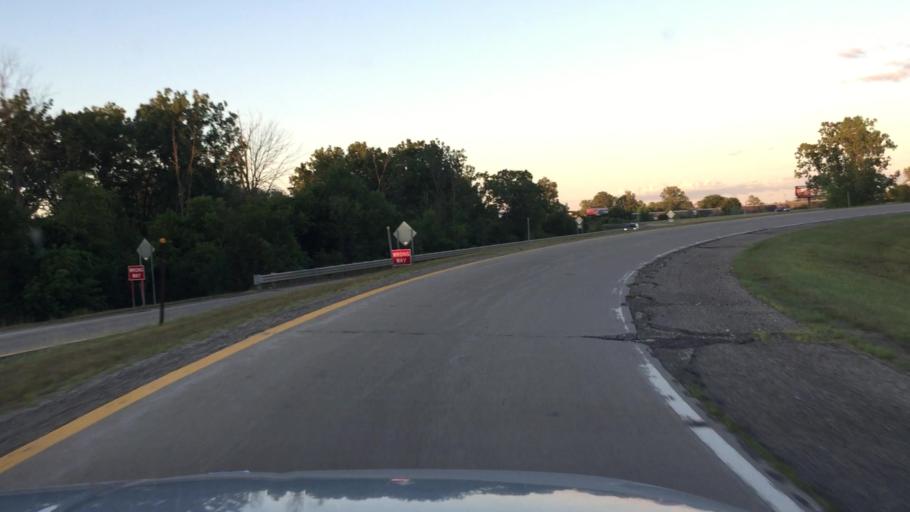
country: US
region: Michigan
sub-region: Genesee County
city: Swartz Creek
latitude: 42.9742
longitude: -83.7664
